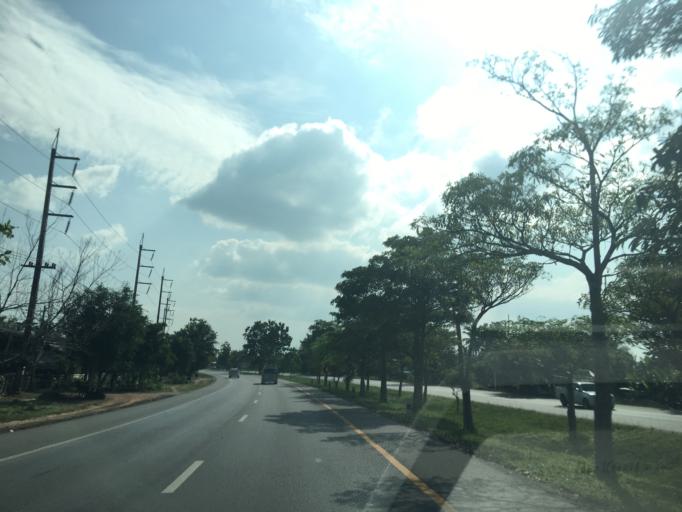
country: TH
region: Chiang Rai
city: Mae Lao
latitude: 19.7284
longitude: 99.7172
